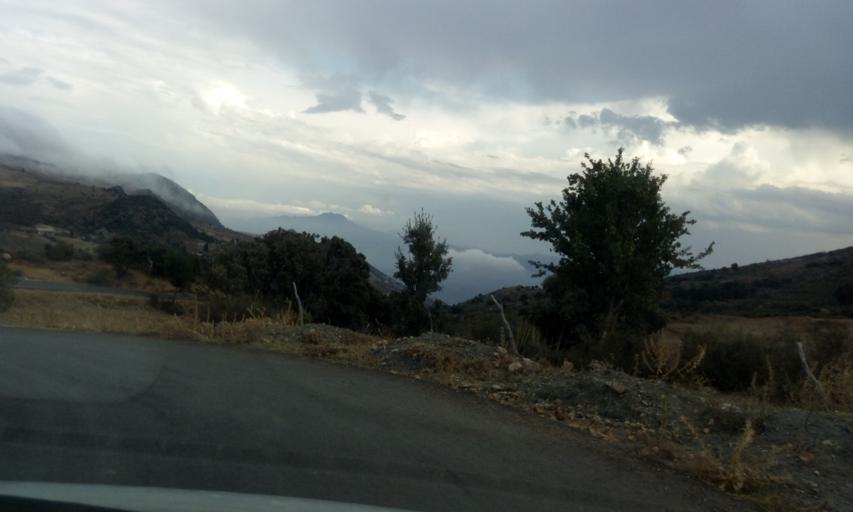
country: DZ
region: Tizi Ouzou
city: Chemini
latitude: 36.6100
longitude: 4.5585
